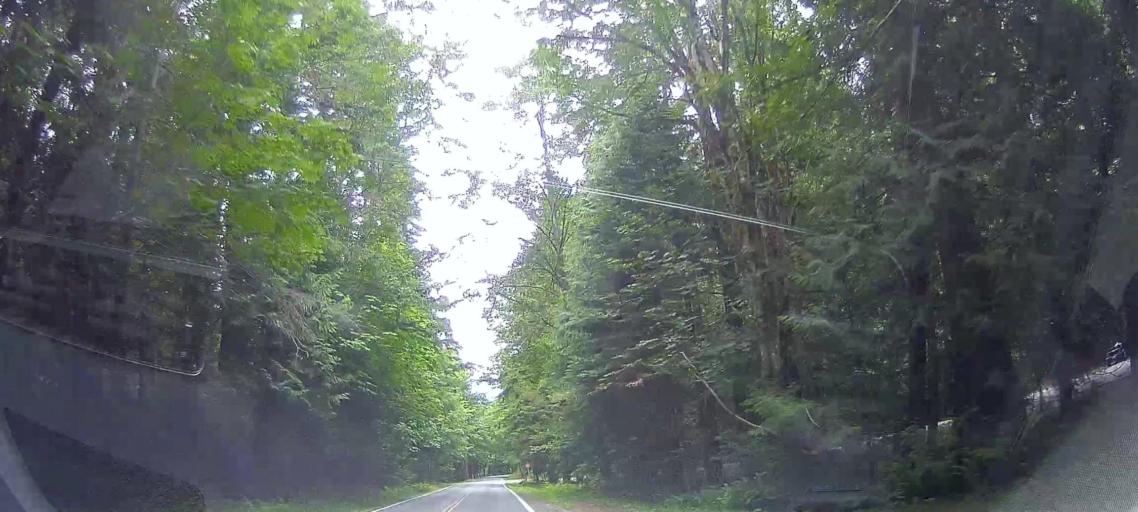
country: US
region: Washington
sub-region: Skagit County
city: Anacortes
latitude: 48.4680
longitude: -122.6303
